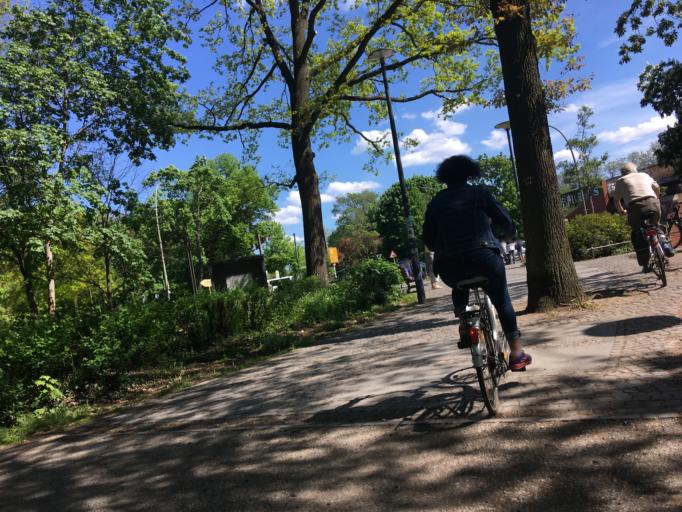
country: DE
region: Berlin
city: Friedrichshagen
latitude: 52.4578
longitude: 13.6248
